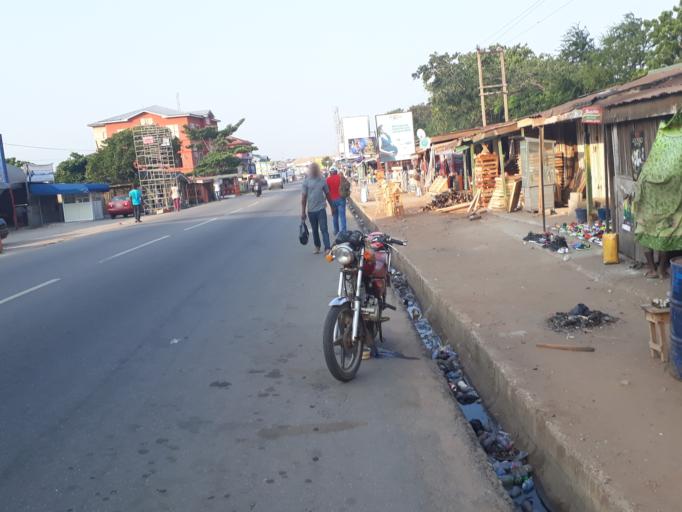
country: GH
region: Greater Accra
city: Dome
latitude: 5.6403
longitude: -0.2410
